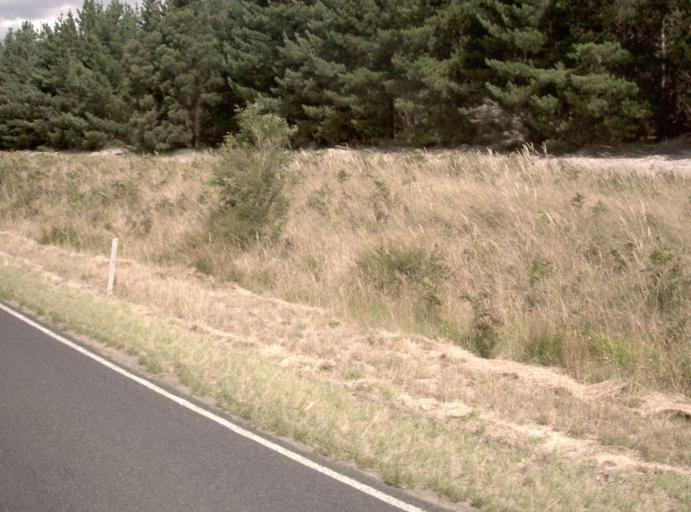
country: AU
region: Victoria
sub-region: Wellington
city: Sale
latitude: -38.1623
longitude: 146.8894
